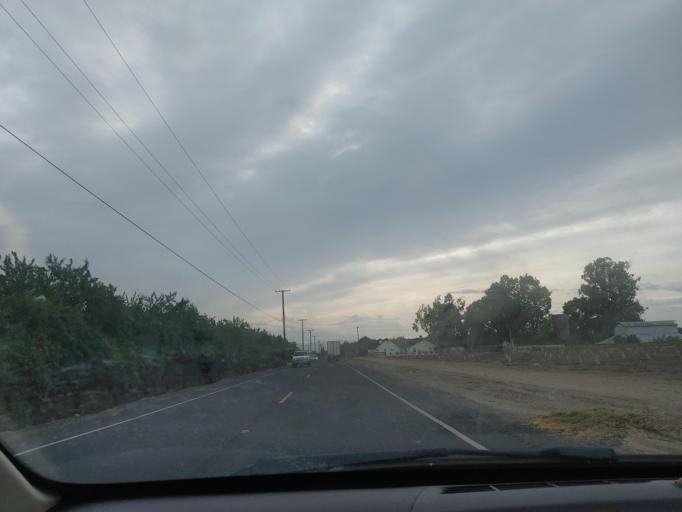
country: US
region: California
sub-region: Stanislaus County
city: Salida
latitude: 37.6814
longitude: -121.1202
